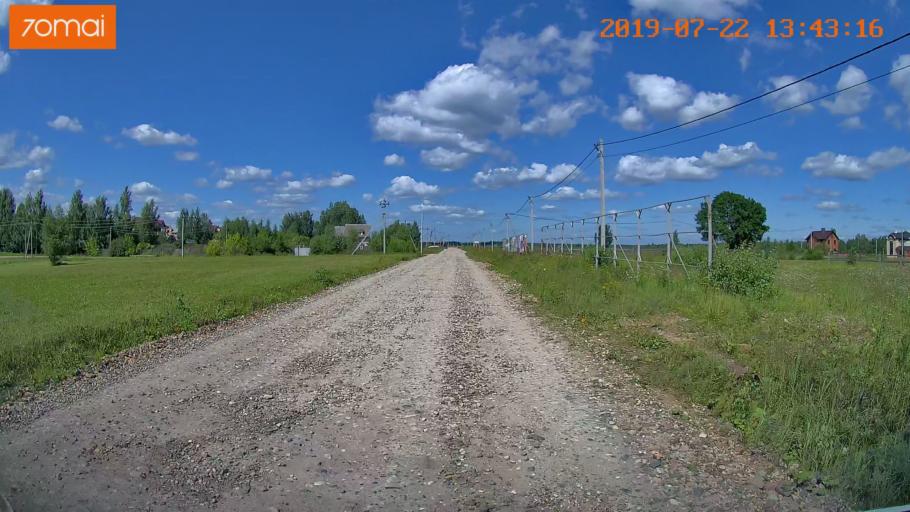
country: RU
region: Ivanovo
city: Novo-Talitsy
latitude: 57.0823
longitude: 40.8744
